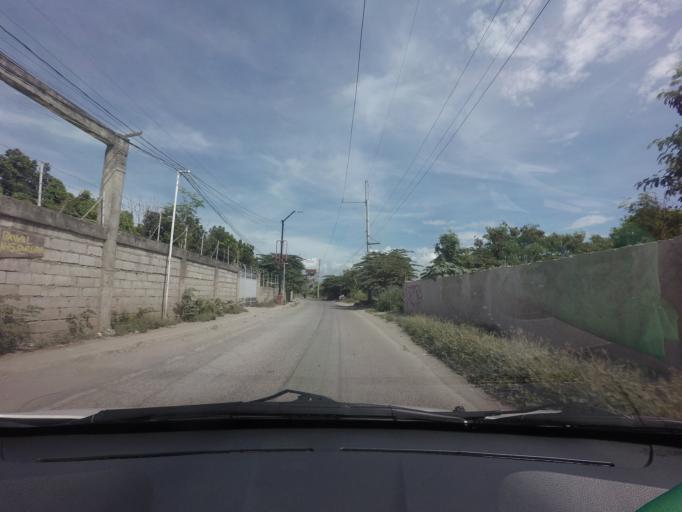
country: PH
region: Calabarzon
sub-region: Province of Rizal
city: Taguig
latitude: 14.5286
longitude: 121.0867
